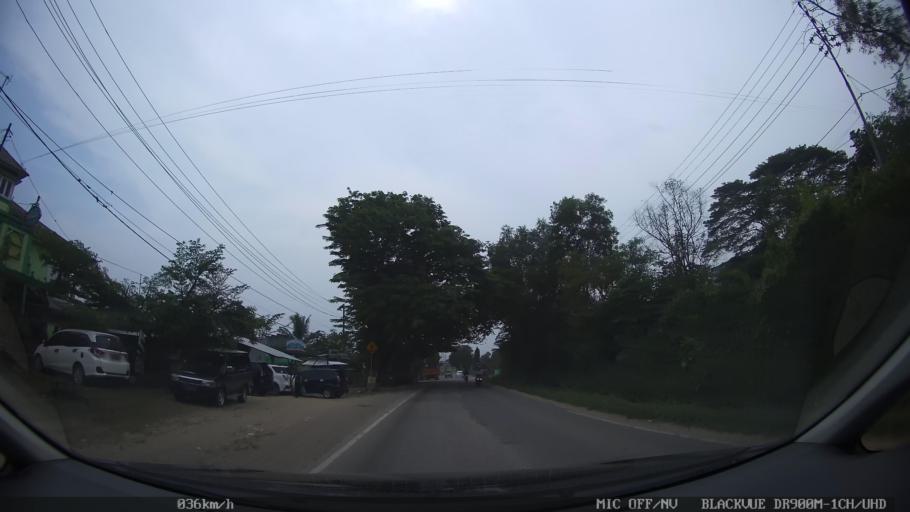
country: ID
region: Lampung
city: Panjang
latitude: -5.4027
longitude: 105.3521
